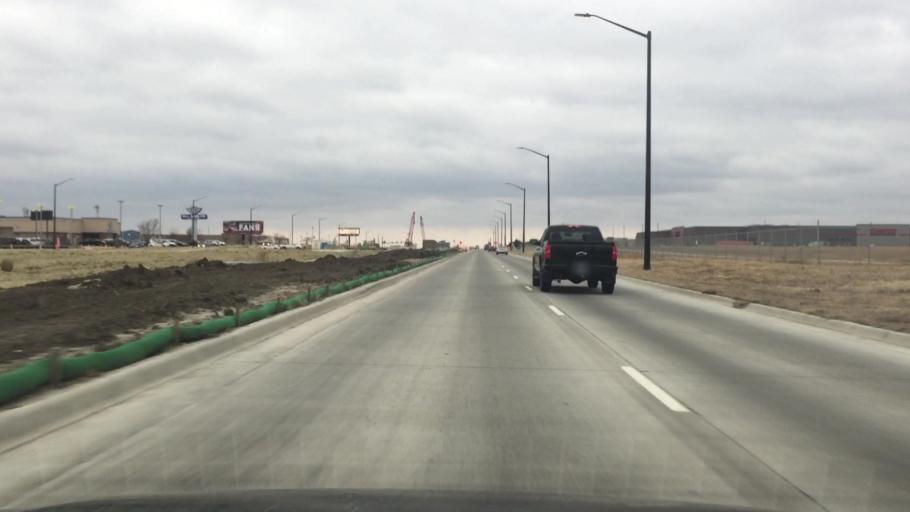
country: US
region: Kansas
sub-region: Butler County
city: Andover
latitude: 37.6794
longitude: -97.2178
